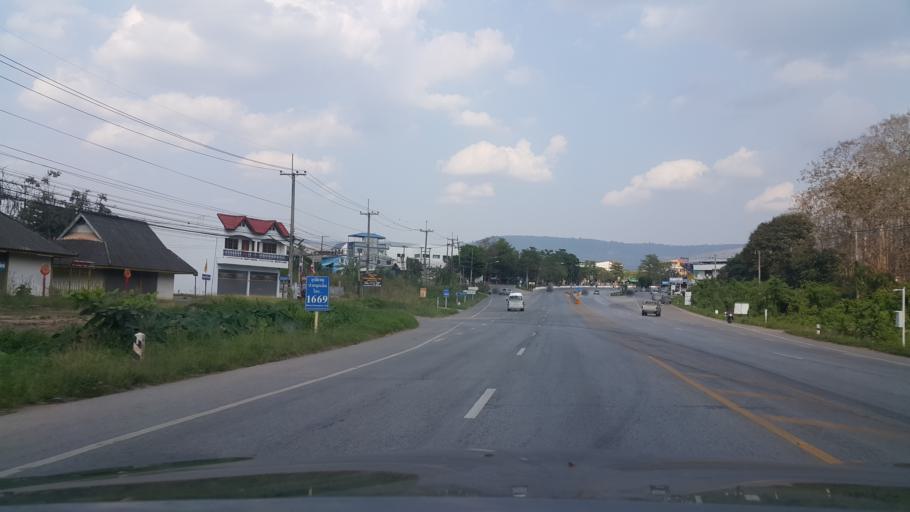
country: TH
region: Phitsanulok
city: Wang Thong
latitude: 16.8679
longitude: 100.6699
